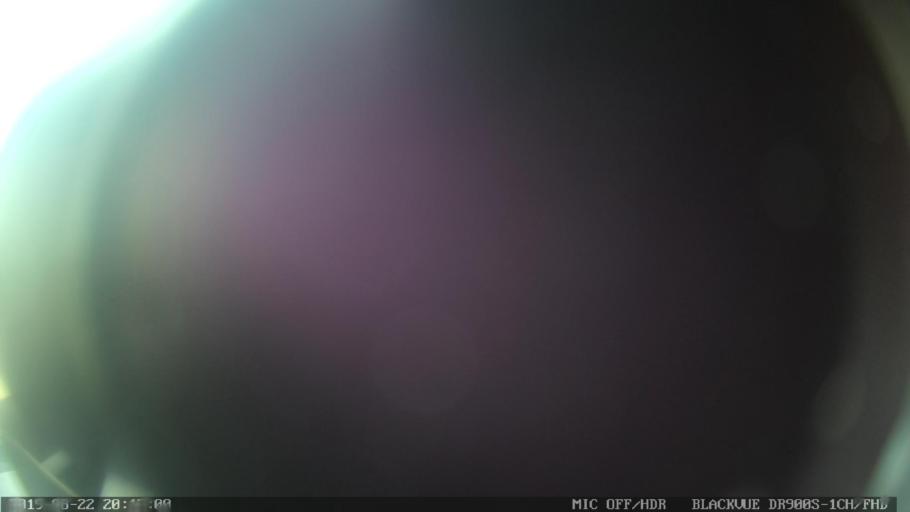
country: PT
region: Guarda
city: Alcains
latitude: 39.9240
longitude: -7.4631
